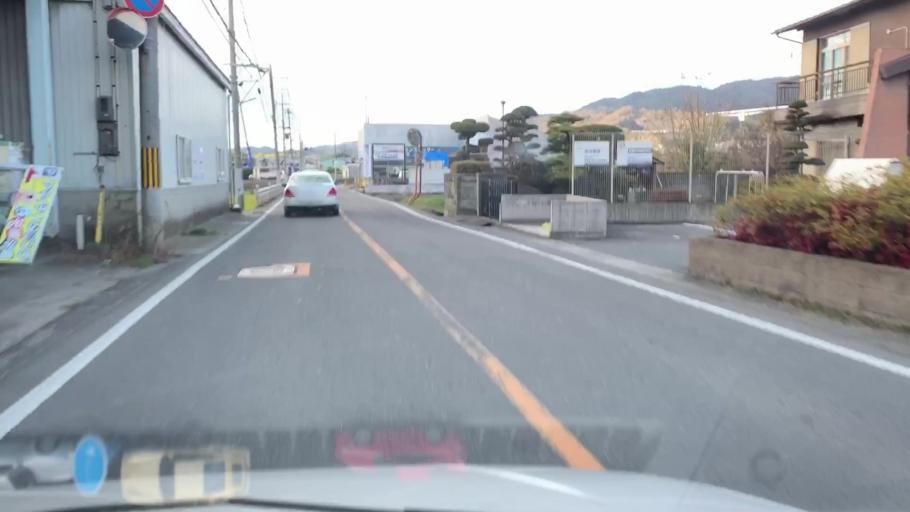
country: JP
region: Wakayama
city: Iwade
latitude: 34.2714
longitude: 135.2678
